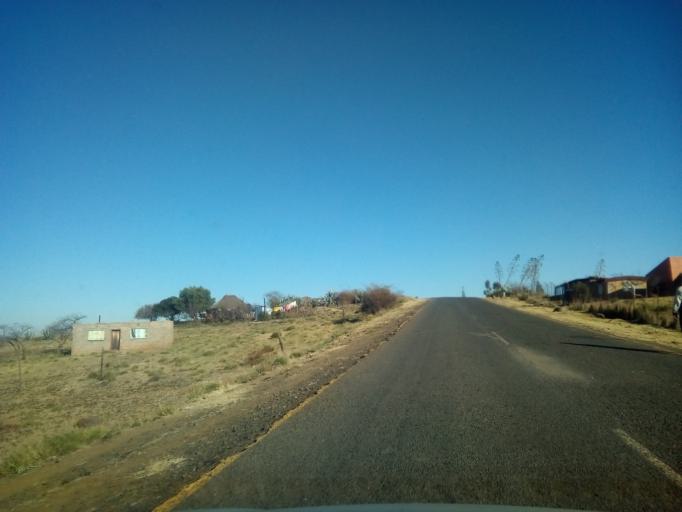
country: LS
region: Berea
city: Teyateyaneng
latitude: -29.2526
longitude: 27.7934
